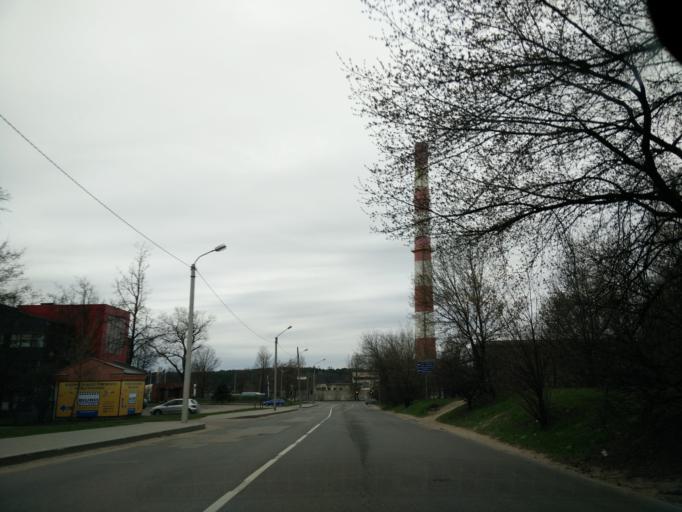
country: LT
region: Vilnius County
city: Vilkpede
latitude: 54.6635
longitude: 25.2385
